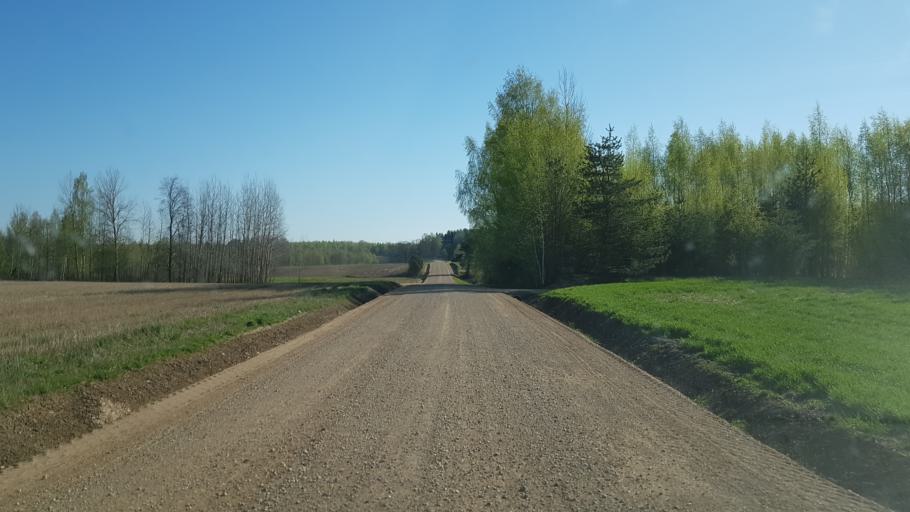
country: EE
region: Polvamaa
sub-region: Polva linn
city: Polva
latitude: 58.1049
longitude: 27.2306
